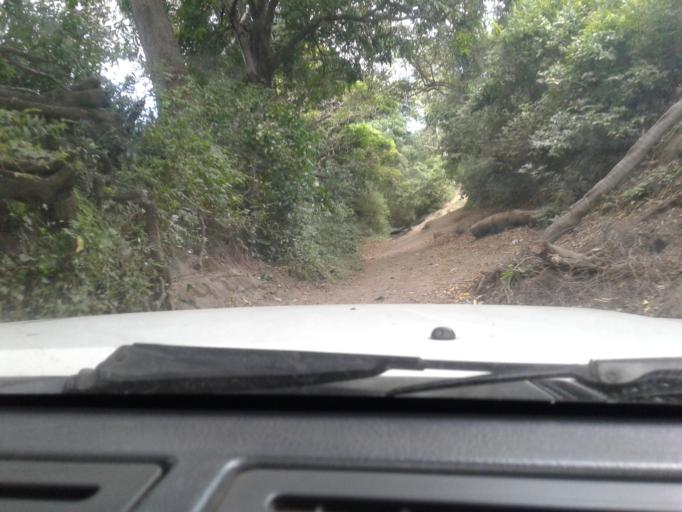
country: NI
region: Rivas
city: Moyogalpa
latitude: 11.4973
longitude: -85.6768
